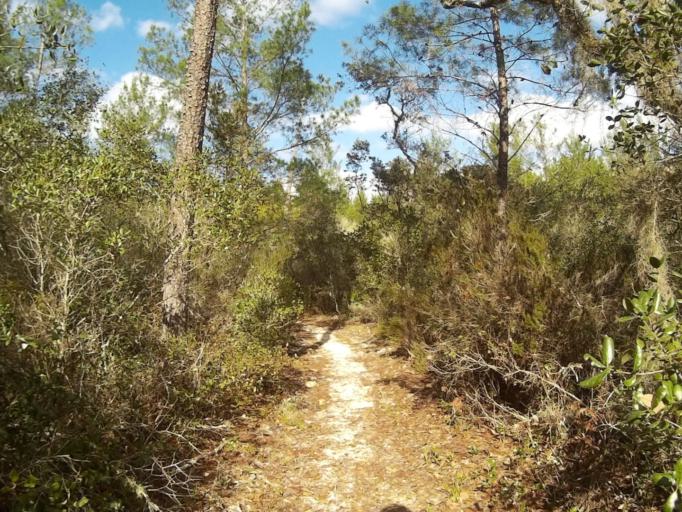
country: US
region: Florida
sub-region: Lake County
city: Astor
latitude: 29.0692
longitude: -81.6155
